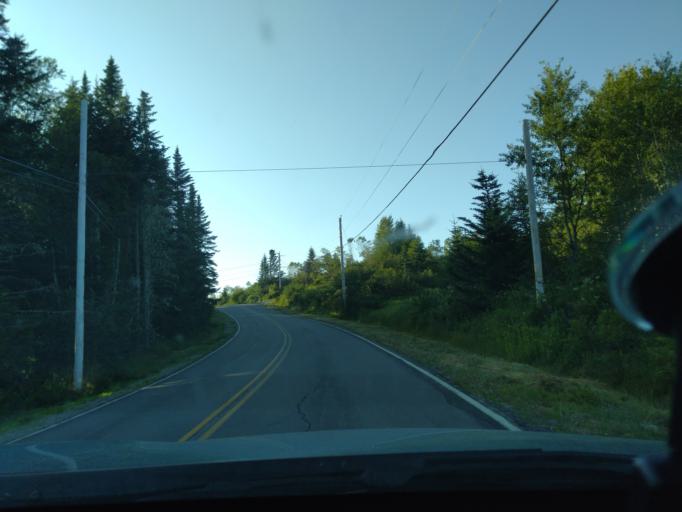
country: US
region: Maine
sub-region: Washington County
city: Machiasport
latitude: 44.6676
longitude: -67.2391
